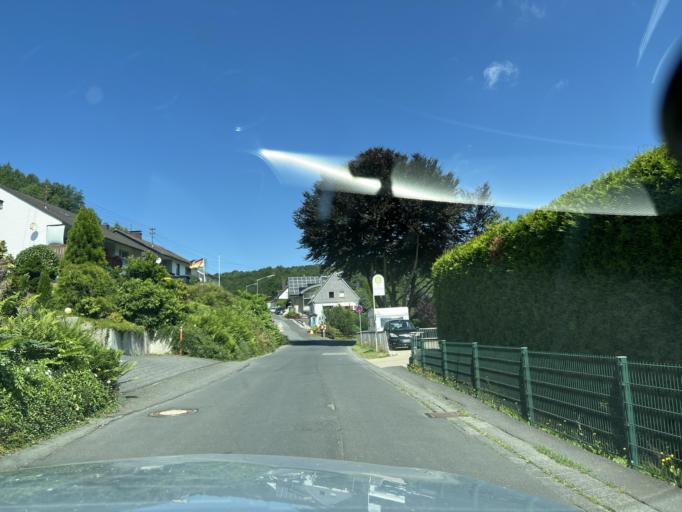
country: DE
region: North Rhine-Westphalia
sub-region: Regierungsbezirk Arnsberg
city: Siegen
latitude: 50.8976
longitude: 7.9820
